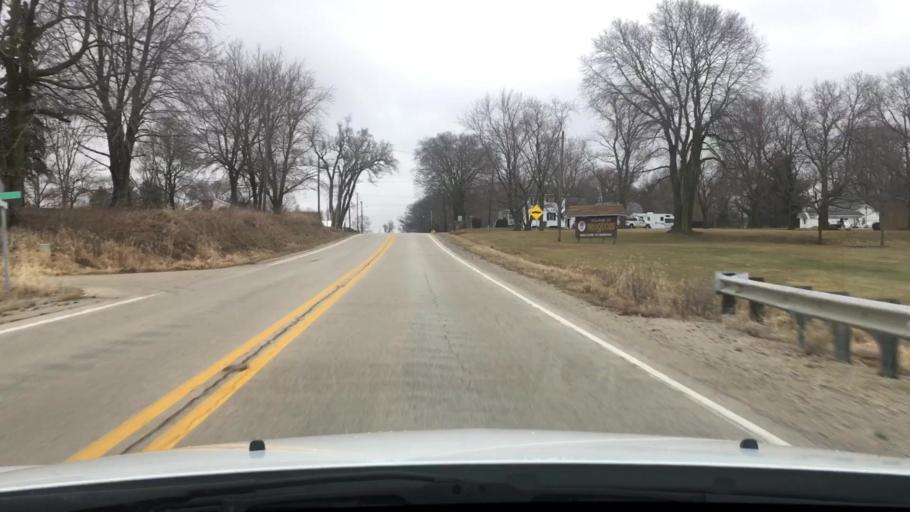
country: US
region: Illinois
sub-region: Iroquois County
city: Sheldon
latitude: 40.8246
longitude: -87.5816
